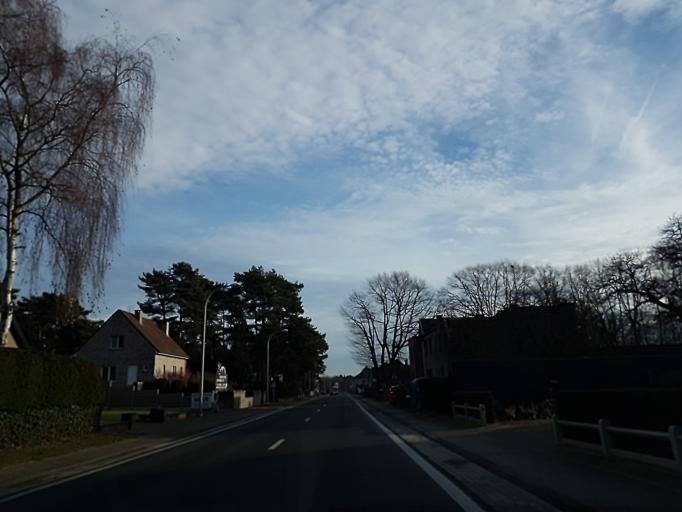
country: BE
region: Flanders
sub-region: Provincie Vlaams-Brabant
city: Tremelo
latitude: 50.9948
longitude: 4.6826
